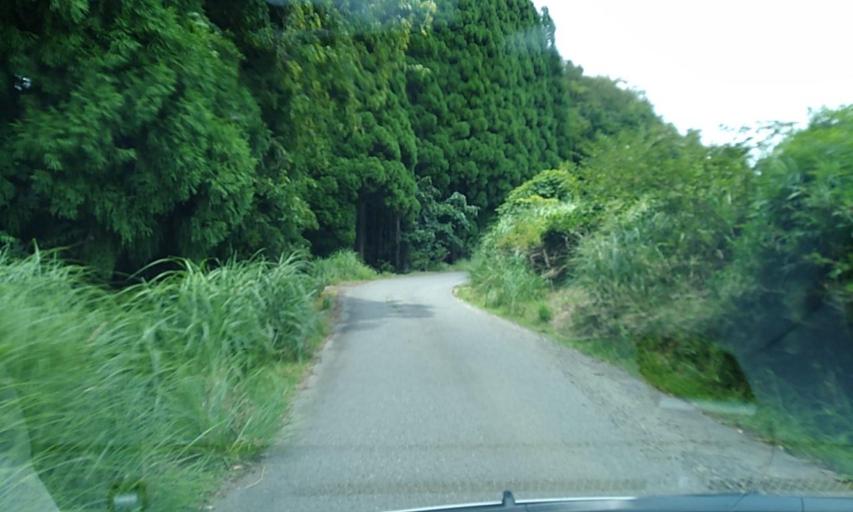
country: JP
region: Kyoto
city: Maizuru
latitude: 35.3798
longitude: 135.4365
